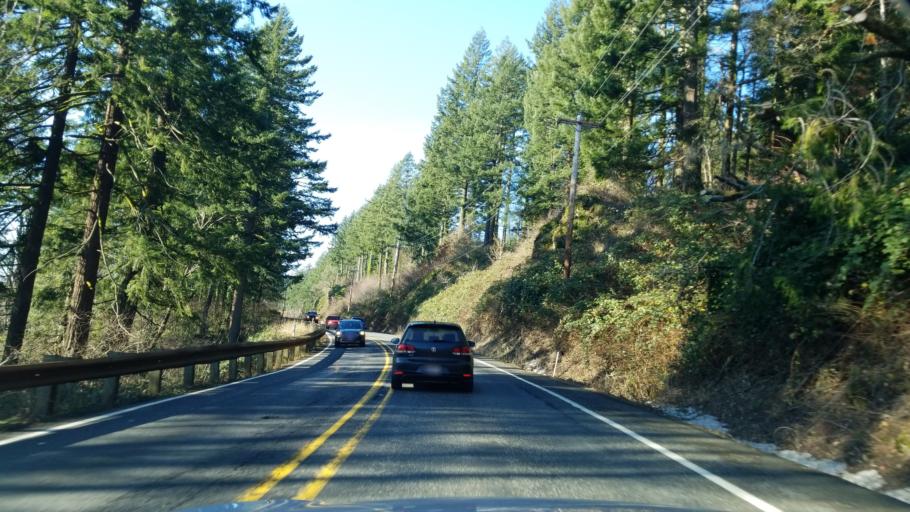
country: US
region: Oregon
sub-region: Hood River County
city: Cascade Locks
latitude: 45.6068
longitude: -122.0862
